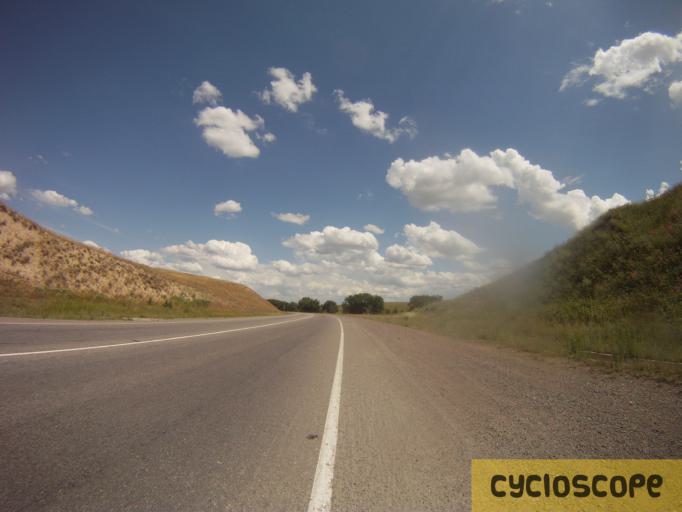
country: KZ
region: Almaty Oblysy
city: Burunday
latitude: 43.3058
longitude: 76.2068
